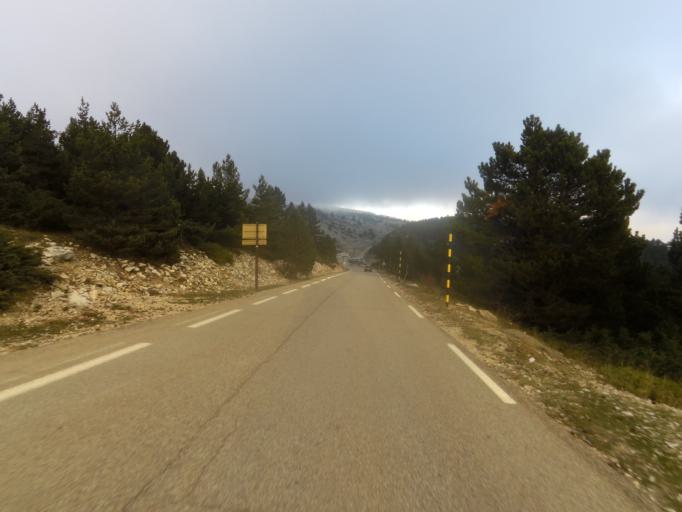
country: FR
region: Provence-Alpes-Cote d'Azur
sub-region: Departement du Vaucluse
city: Sault
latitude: 44.1511
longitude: 5.3151
